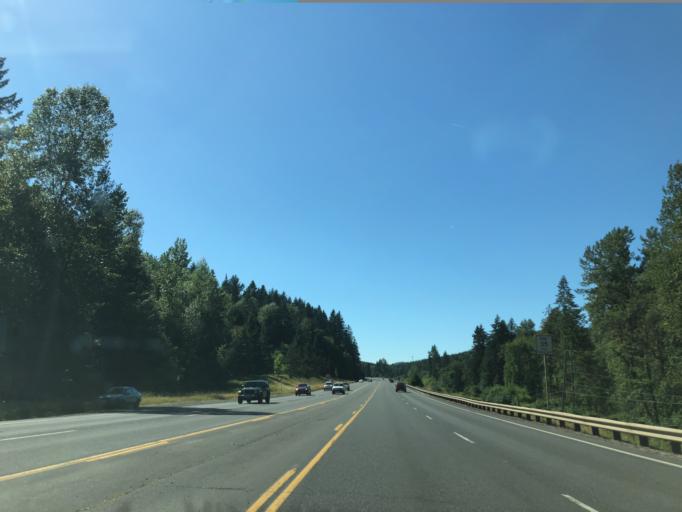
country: US
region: Oregon
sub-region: Linn County
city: Sweet Home
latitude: 44.4009
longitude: -122.7438
